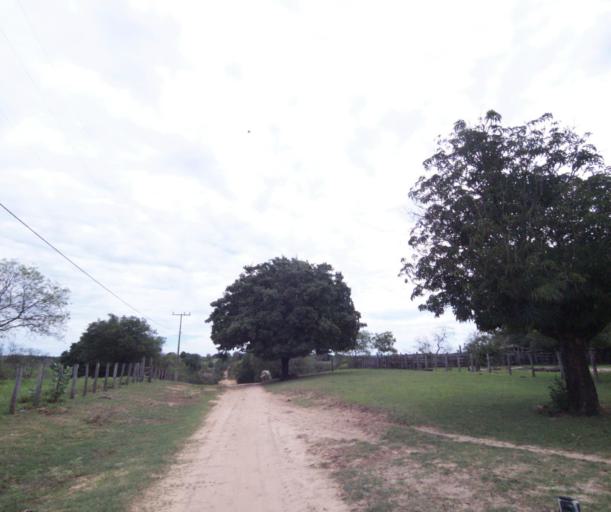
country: BR
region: Bahia
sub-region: Carinhanha
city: Carinhanha
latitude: -14.2498
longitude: -44.3505
